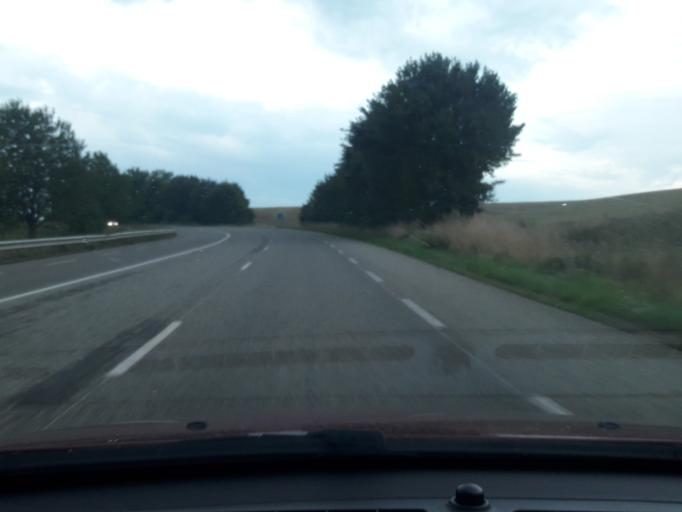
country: FR
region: Alsace
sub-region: Departement du Bas-Rhin
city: Dauendorf
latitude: 48.8126
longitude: 7.6332
